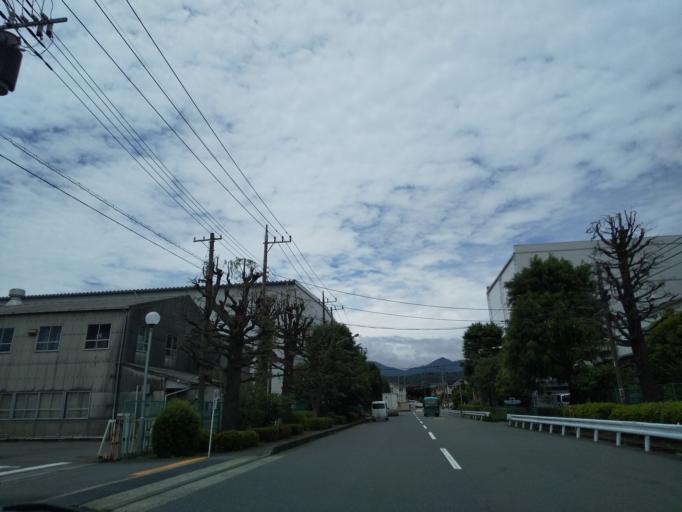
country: JP
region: Kanagawa
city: Zama
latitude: 35.5195
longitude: 139.3407
